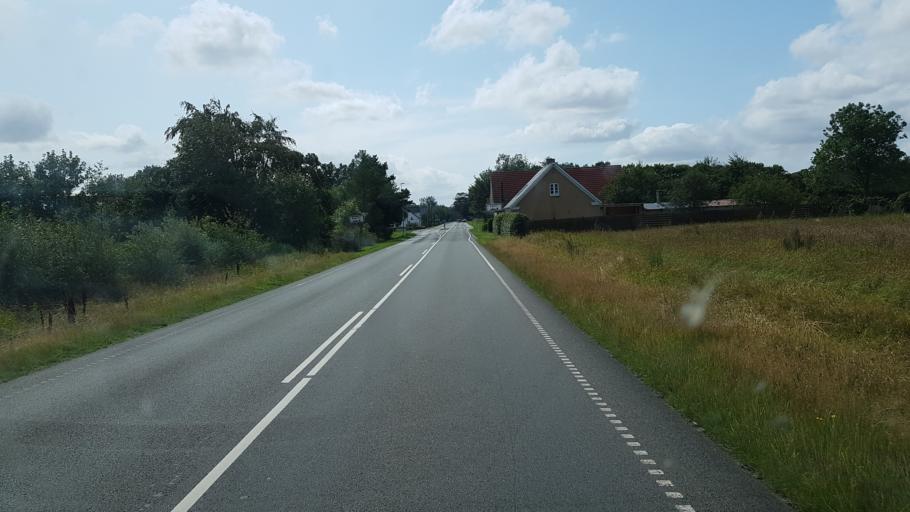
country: DK
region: South Denmark
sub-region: Vejen Kommune
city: Vejen
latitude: 55.5748
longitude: 9.1535
